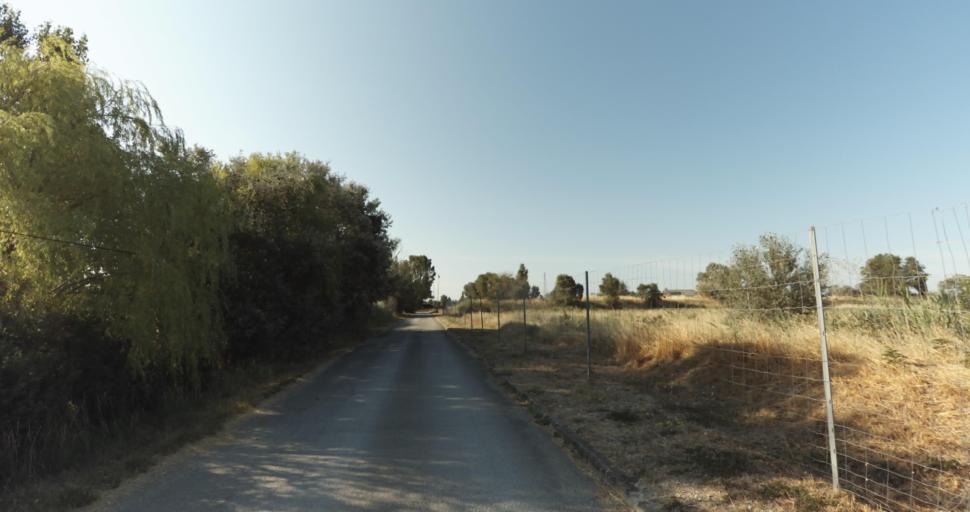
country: FR
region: Provence-Alpes-Cote d'Azur
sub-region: Departement du Vaucluse
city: Sarrians
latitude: 44.0541
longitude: 4.9477
